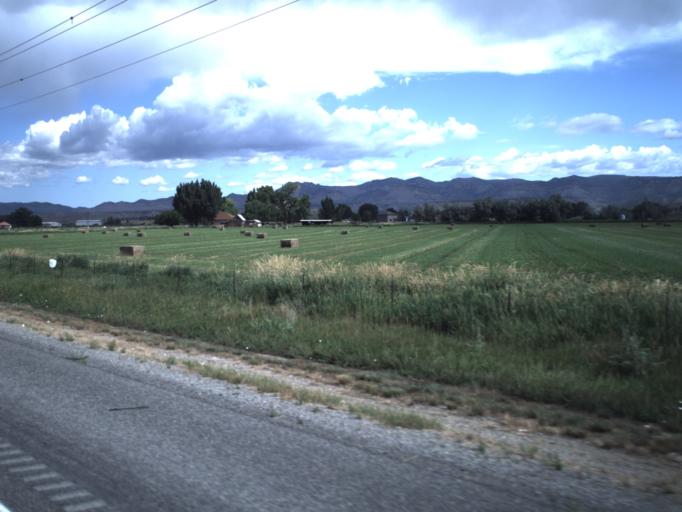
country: US
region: Utah
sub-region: Carbon County
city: Price
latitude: 39.5675
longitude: -110.7763
